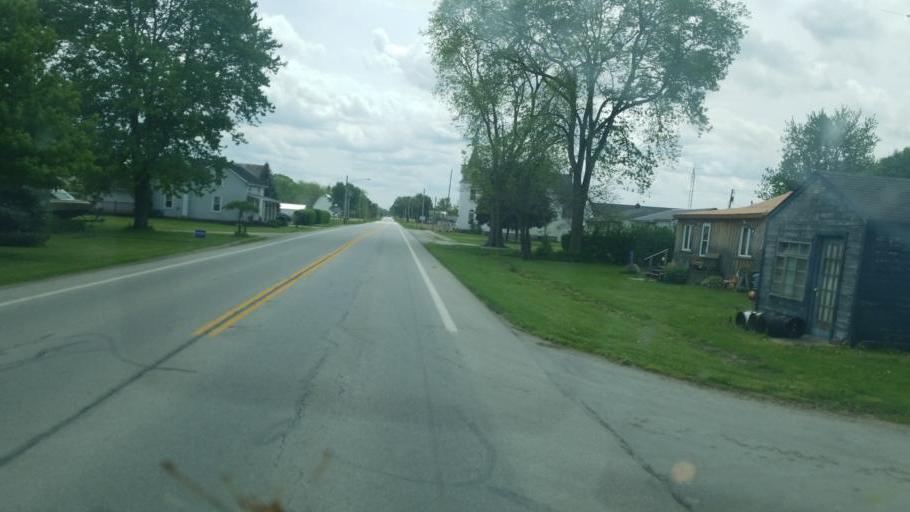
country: US
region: Ohio
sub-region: Seneca County
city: Tiffin
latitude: 41.2076
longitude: -83.1676
